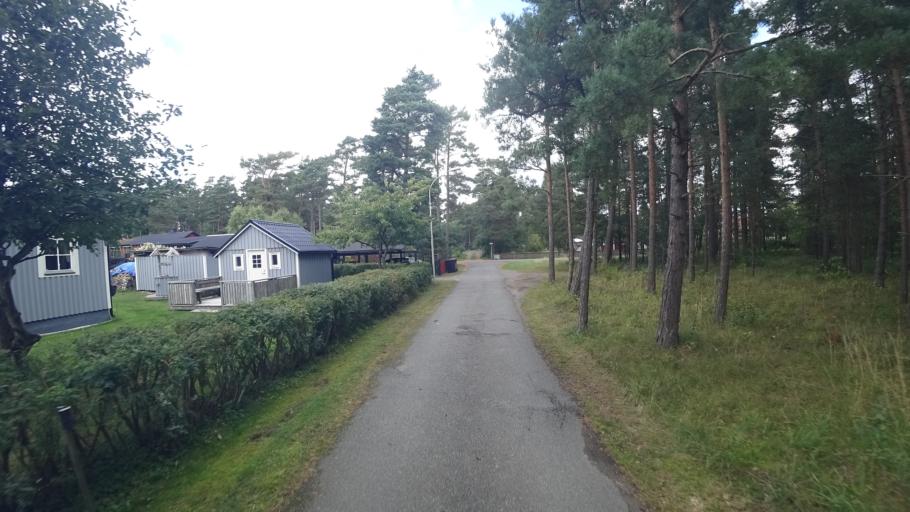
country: SE
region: Skane
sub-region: Kristianstads Kommun
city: Ahus
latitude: 55.9345
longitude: 14.3108
